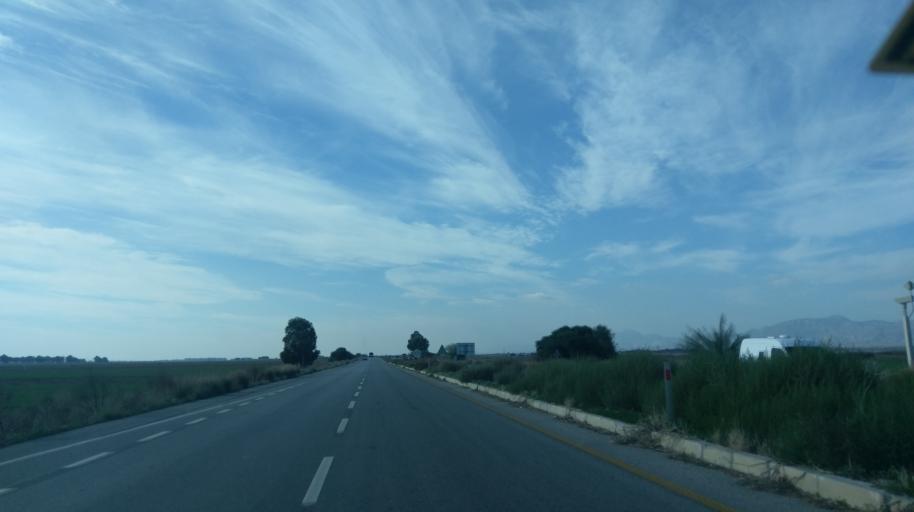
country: CY
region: Ammochostos
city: Lefkonoiko
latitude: 35.1872
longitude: 33.6387
